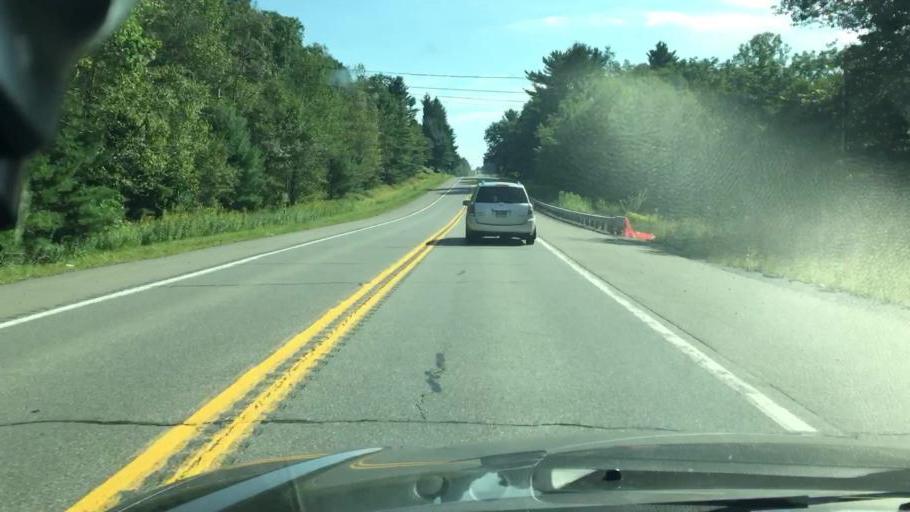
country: US
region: Pennsylvania
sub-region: Carbon County
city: Towamensing Trails
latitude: 40.9641
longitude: -75.6463
